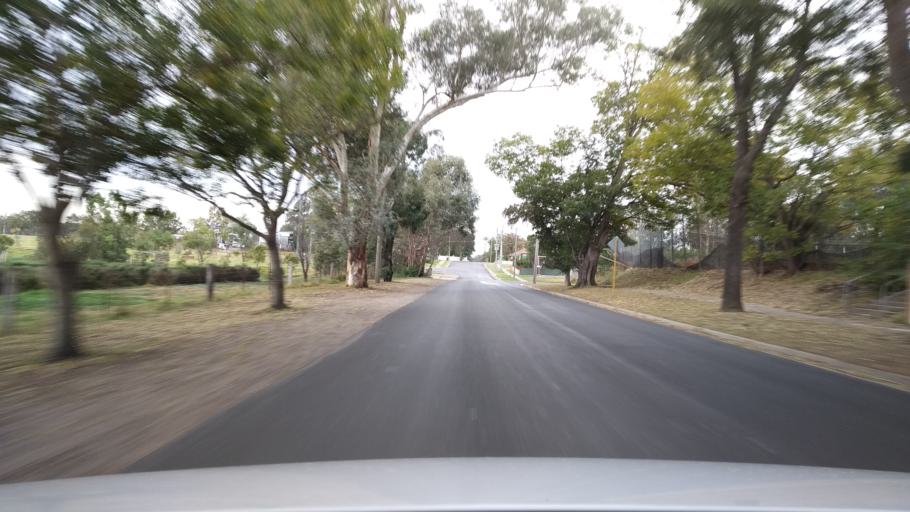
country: AU
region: New South Wales
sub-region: Camden
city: Elderslie
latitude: -34.0503
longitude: 150.6949
